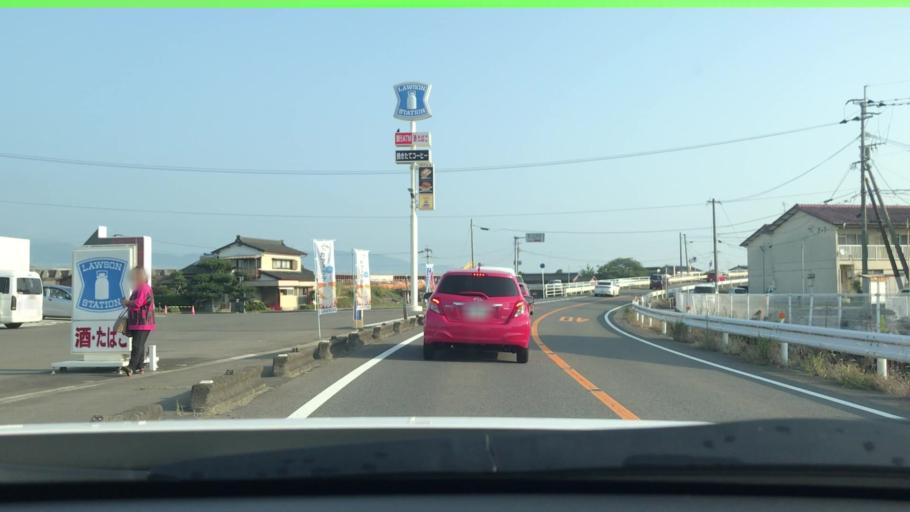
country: JP
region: Saga Prefecture
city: Saga-shi
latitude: 33.1982
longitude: 130.1934
